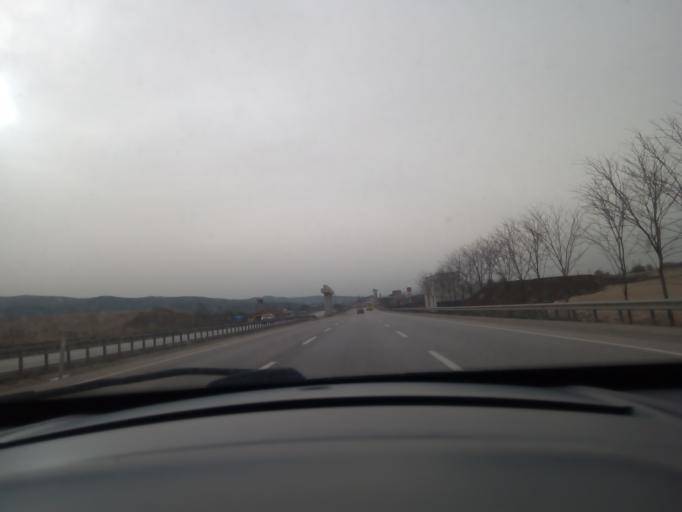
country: TR
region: Balikesir
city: Susurluk
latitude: 39.9593
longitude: 28.1706
